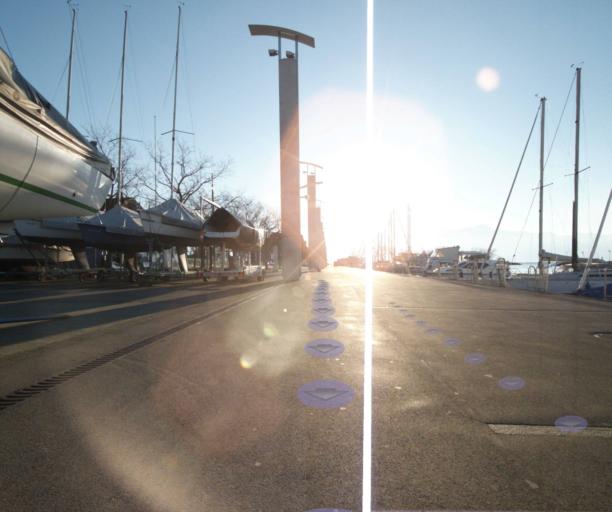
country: CH
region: Vaud
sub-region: Lausanne District
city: Lausanne
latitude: 46.5075
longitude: 6.6240
